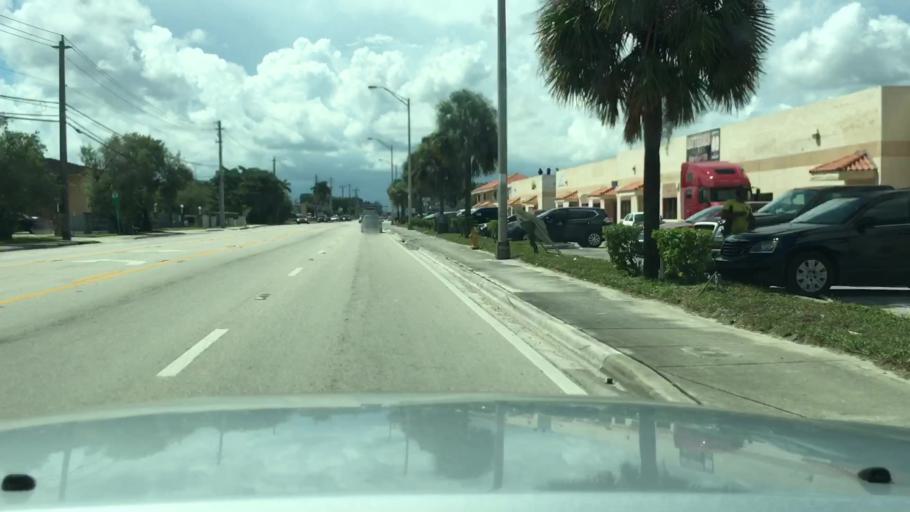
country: US
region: Florida
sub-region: Miami-Dade County
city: Opa-locka
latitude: 25.8966
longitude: -80.2639
